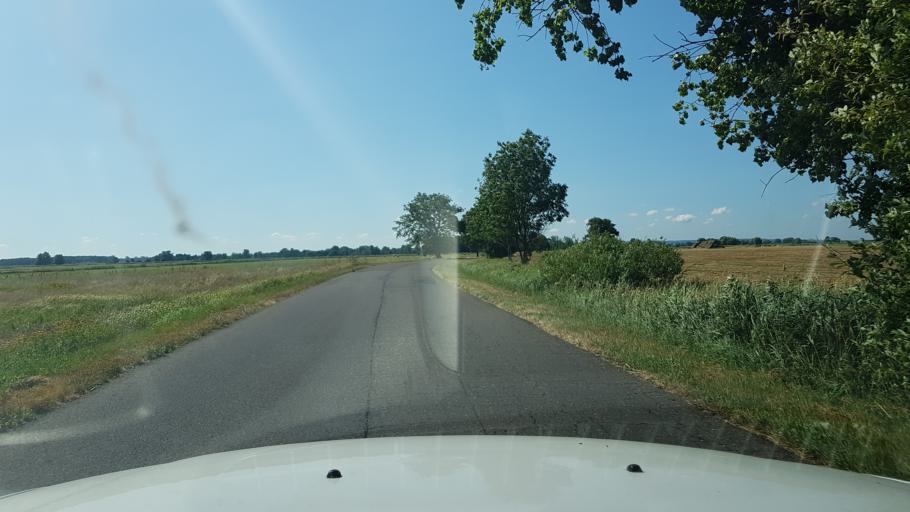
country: PL
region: West Pomeranian Voivodeship
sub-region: Powiat goleniowski
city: Goleniow
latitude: 53.4908
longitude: 14.7125
